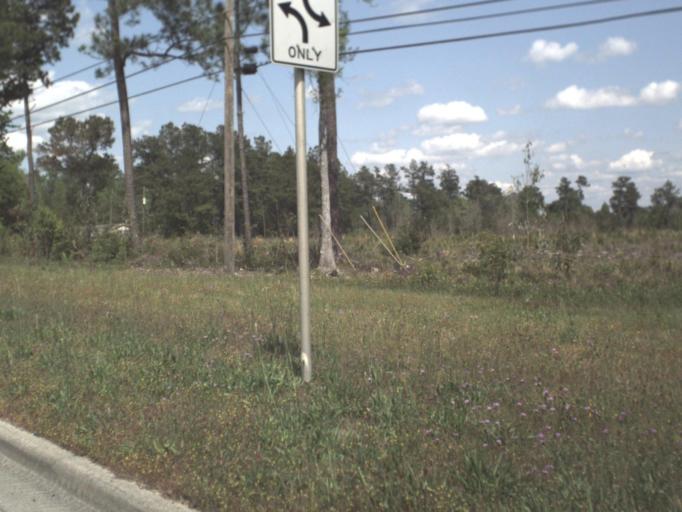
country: US
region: Florida
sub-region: Escambia County
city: Century
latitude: 30.9584
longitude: -87.2764
